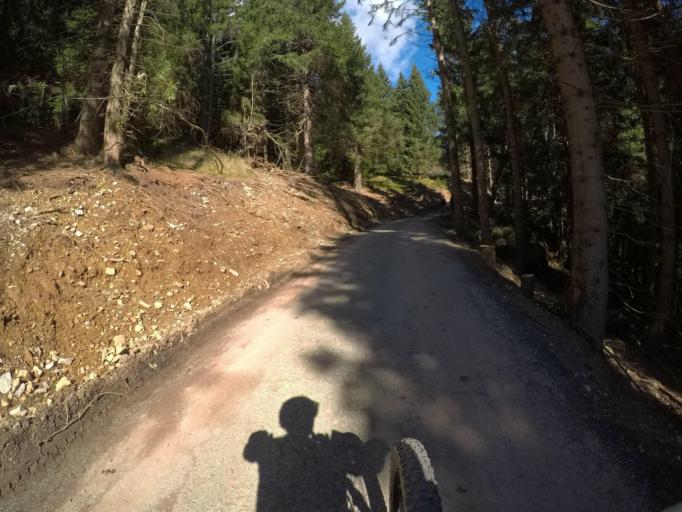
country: IT
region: Friuli Venezia Giulia
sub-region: Provincia di Udine
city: Ligosullo
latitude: 46.5526
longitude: 13.0939
